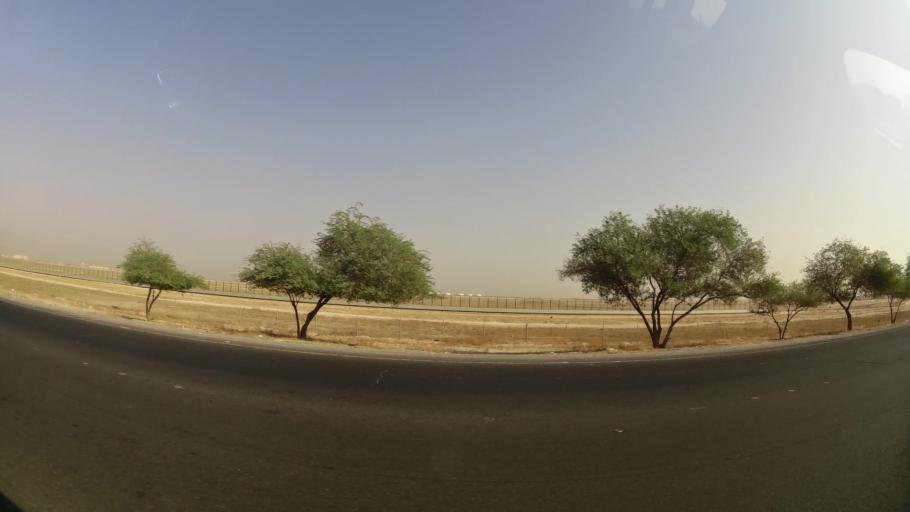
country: KW
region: Al Farwaniyah
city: Janub as Surrah
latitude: 29.1807
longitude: 47.9838
